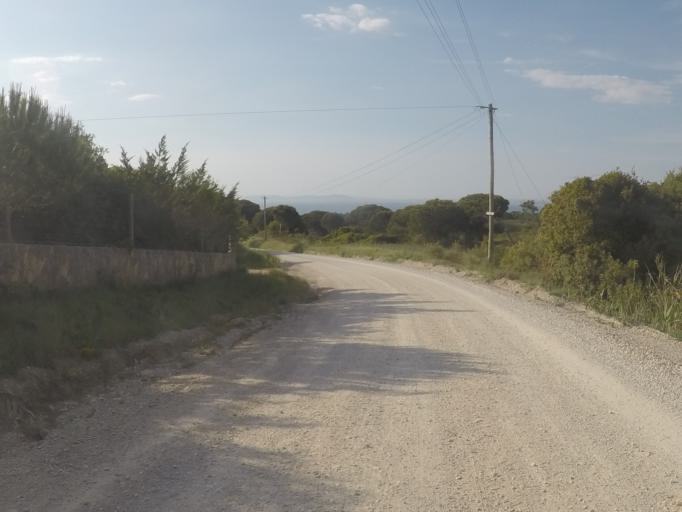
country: PT
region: Setubal
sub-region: Sesimbra
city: Sesimbra
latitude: 38.4366
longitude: -9.1883
